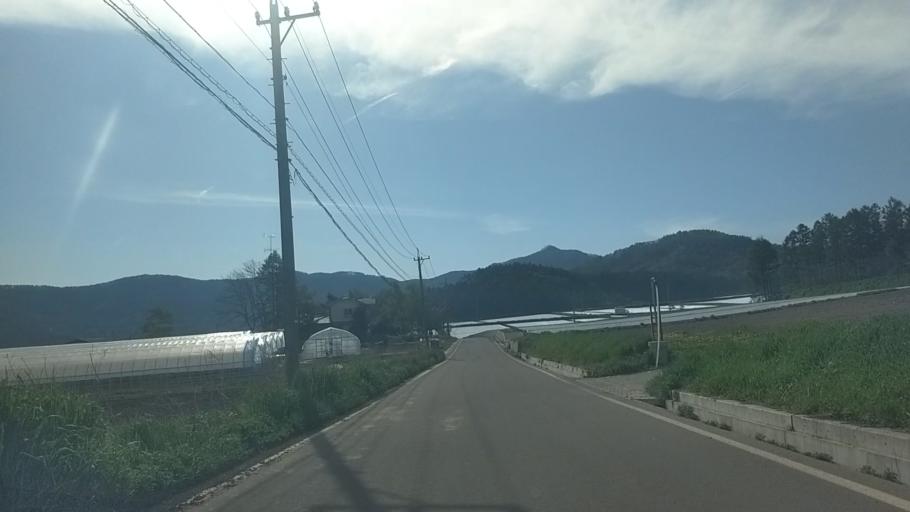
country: JP
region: Yamanashi
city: Nirasaki
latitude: 35.9365
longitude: 138.4707
